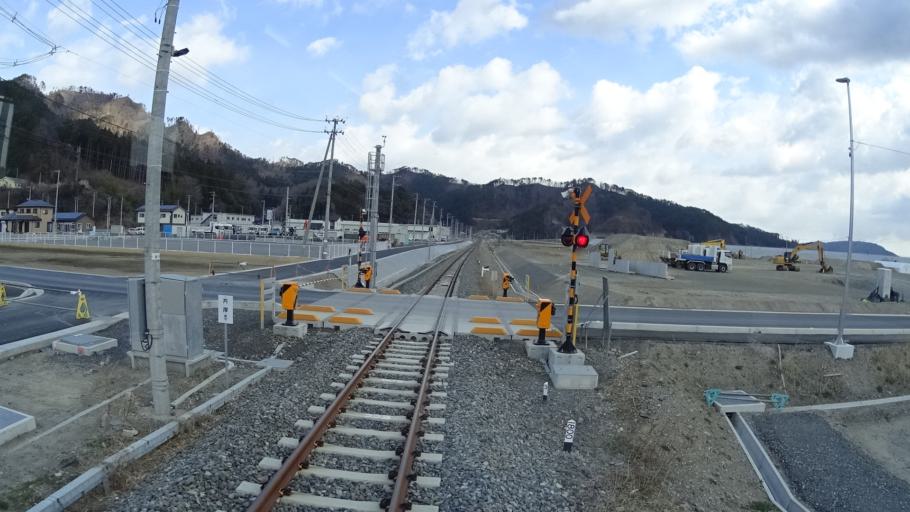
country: JP
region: Iwate
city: Otsuchi
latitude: 39.3325
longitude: 141.8907
